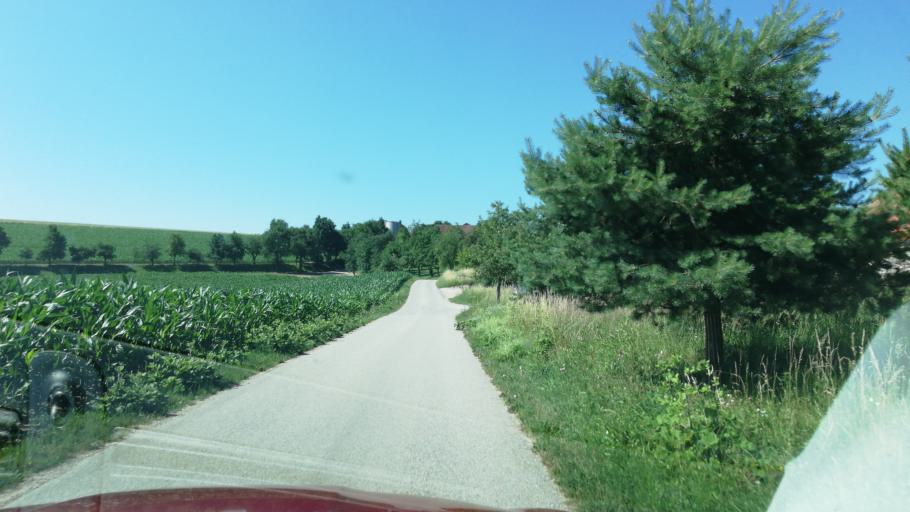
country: AT
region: Upper Austria
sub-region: Politischer Bezirk Grieskirchen
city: Bad Schallerbach
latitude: 48.1834
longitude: 13.9329
